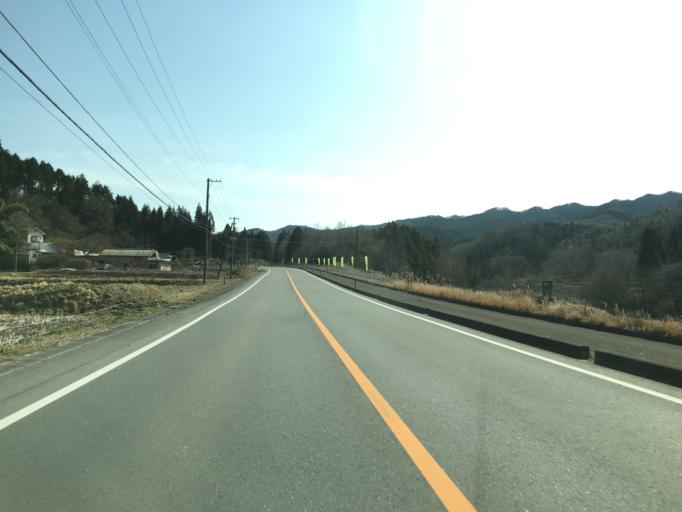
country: JP
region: Ibaraki
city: Daigo
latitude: 36.8229
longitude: 140.4586
